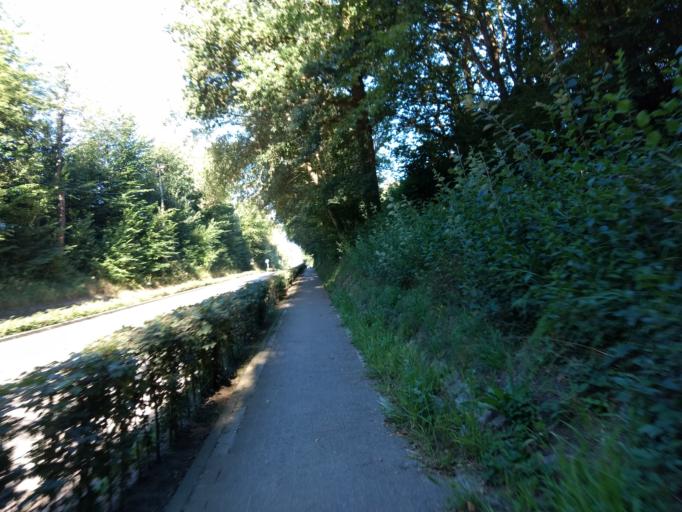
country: BE
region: Flanders
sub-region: Provincie Vlaams-Brabant
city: Bierbeek
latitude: 50.8340
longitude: 4.7453
